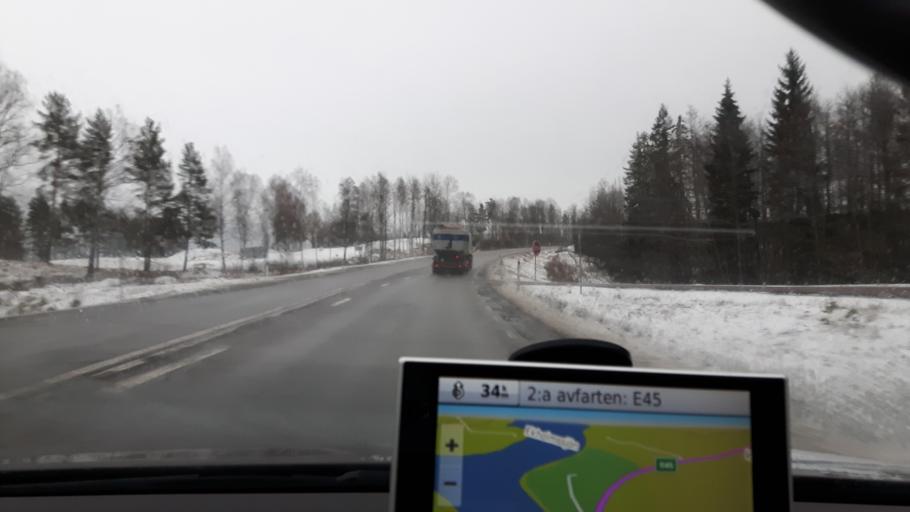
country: SE
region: Vaermland
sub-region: Grums Kommun
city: Slottsbron
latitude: 59.2544
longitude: 12.9999
